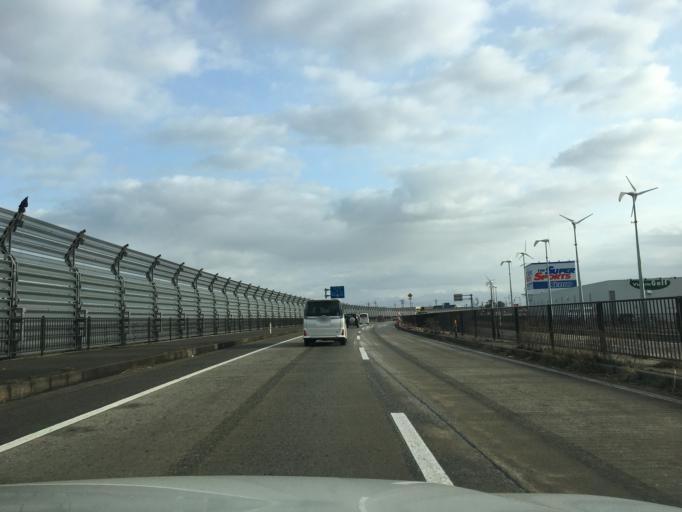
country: JP
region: Yamagata
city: Sakata
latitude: 38.8202
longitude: 139.8330
